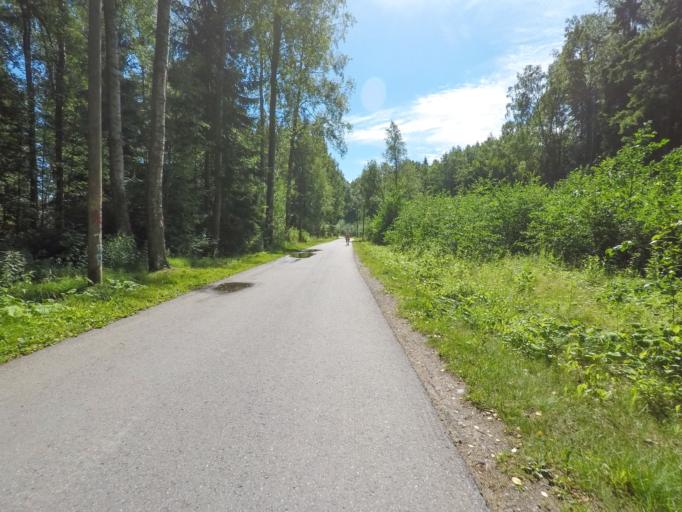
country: FI
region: Uusimaa
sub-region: Helsinki
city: Vantaa
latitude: 60.2165
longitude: 25.0698
